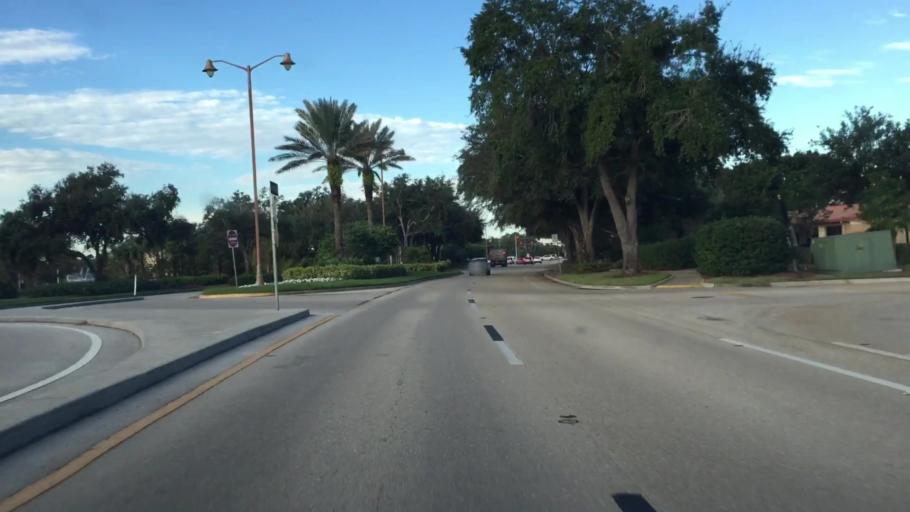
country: US
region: Florida
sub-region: Lee County
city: Estero
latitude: 26.3982
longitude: -81.8080
